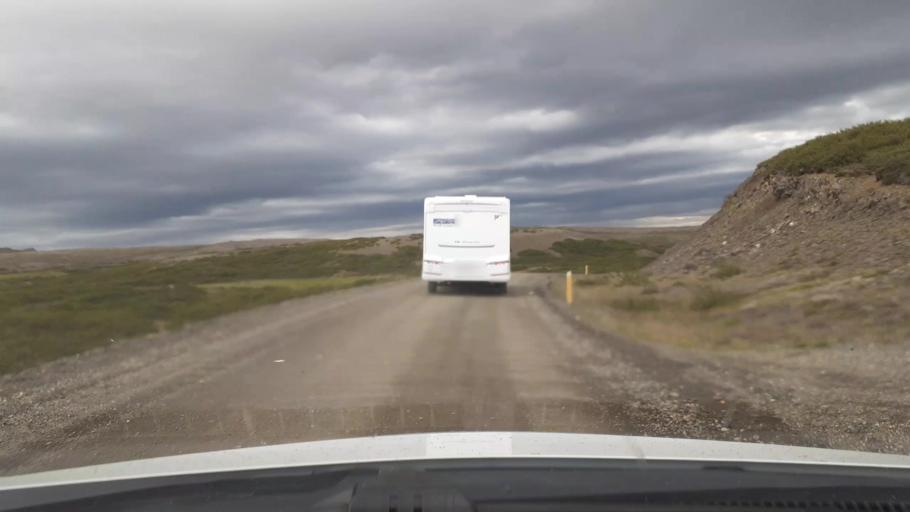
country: IS
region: West
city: Borgarnes
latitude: 64.5585
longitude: -21.6258
